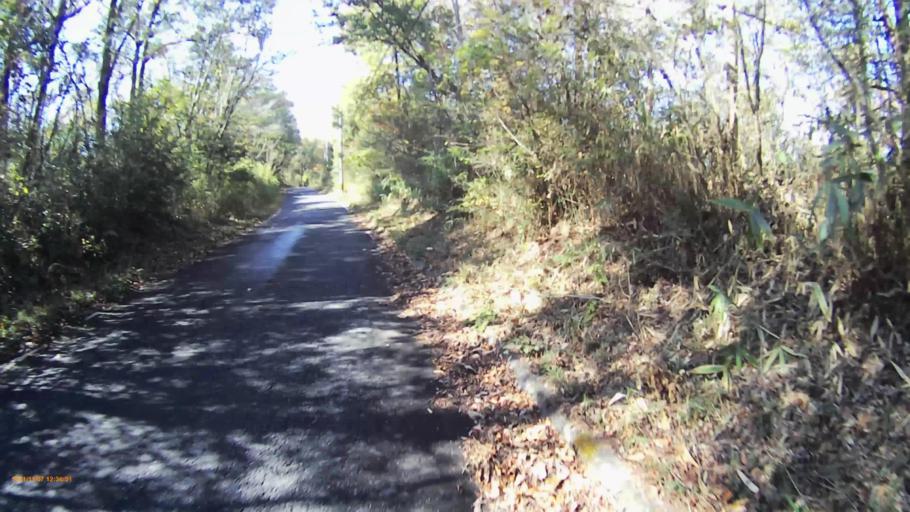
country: JP
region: Gifu
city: Mizunami
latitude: 35.4325
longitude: 137.2488
